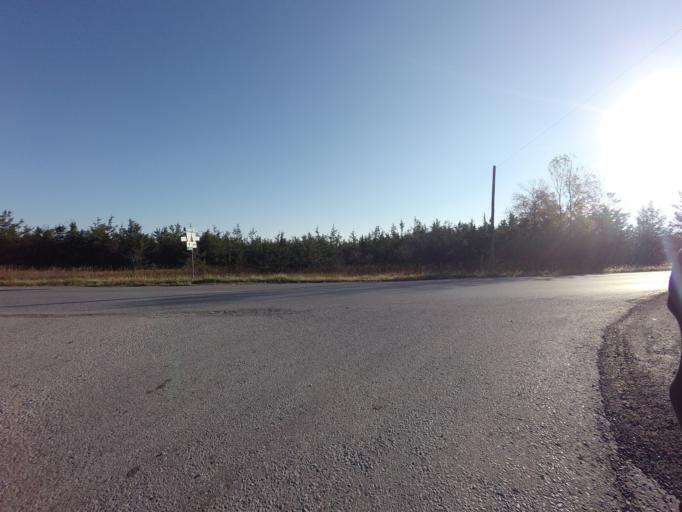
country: CA
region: Ontario
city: Belleville
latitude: 44.0623
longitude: -77.3978
